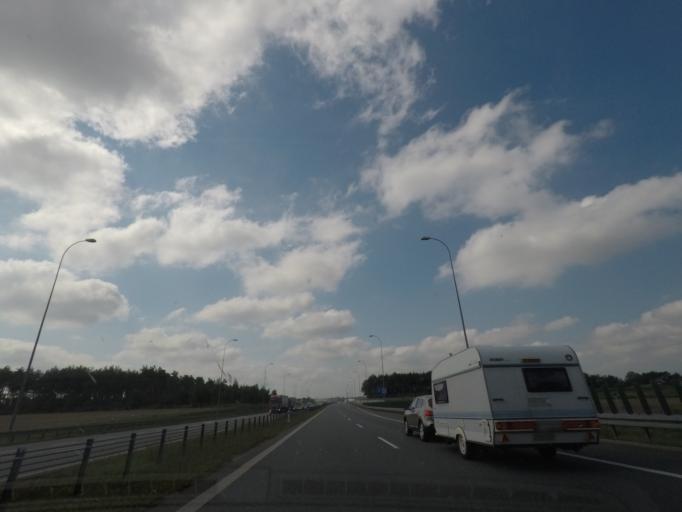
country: PL
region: Kujawsko-Pomorskie
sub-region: Powiat torunski
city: Lubicz Dolny
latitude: 53.1467
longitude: 18.7441
